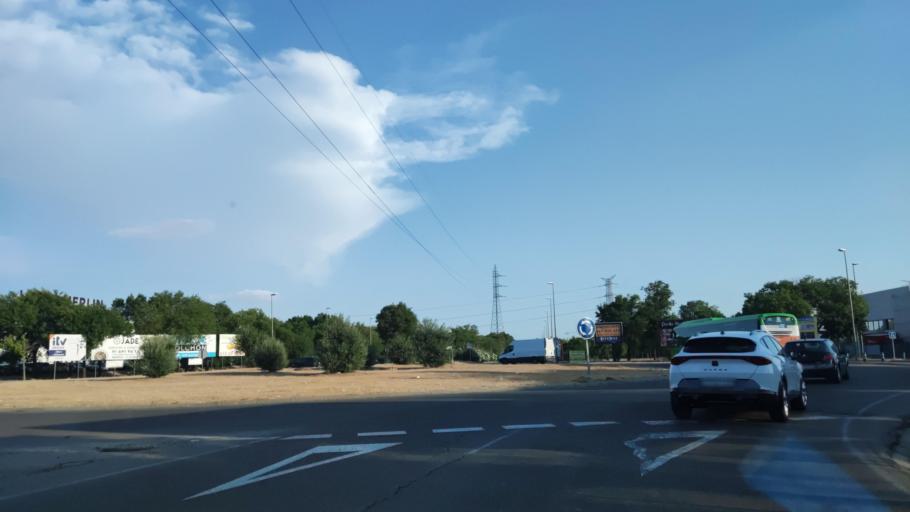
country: ES
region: Madrid
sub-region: Provincia de Madrid
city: Pinto
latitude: 40.2713
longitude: -3.7000
